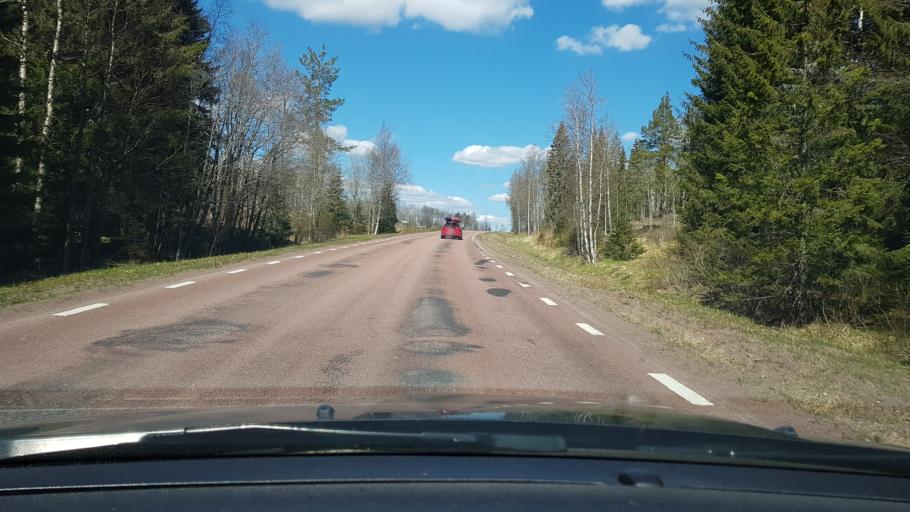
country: SE
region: Dalarna
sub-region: Alvdalens Kommun
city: AElvdalen
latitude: 61.1263
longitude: 13.9684
